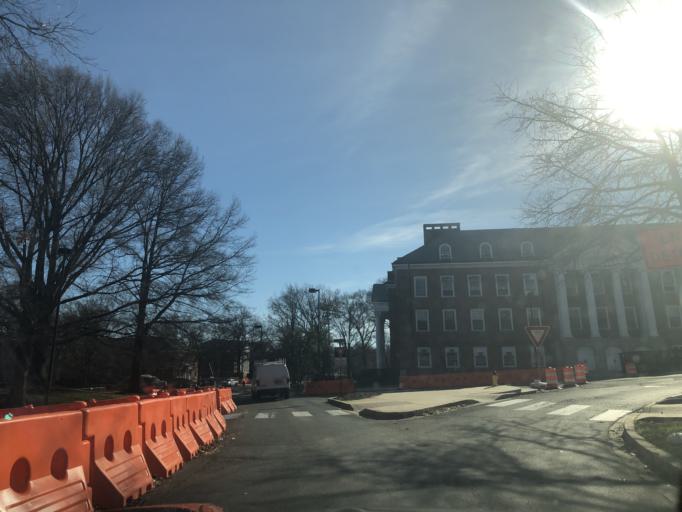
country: US
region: Maryland
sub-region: Prince George's County
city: College Park
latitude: 38.9880
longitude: -76.9407
